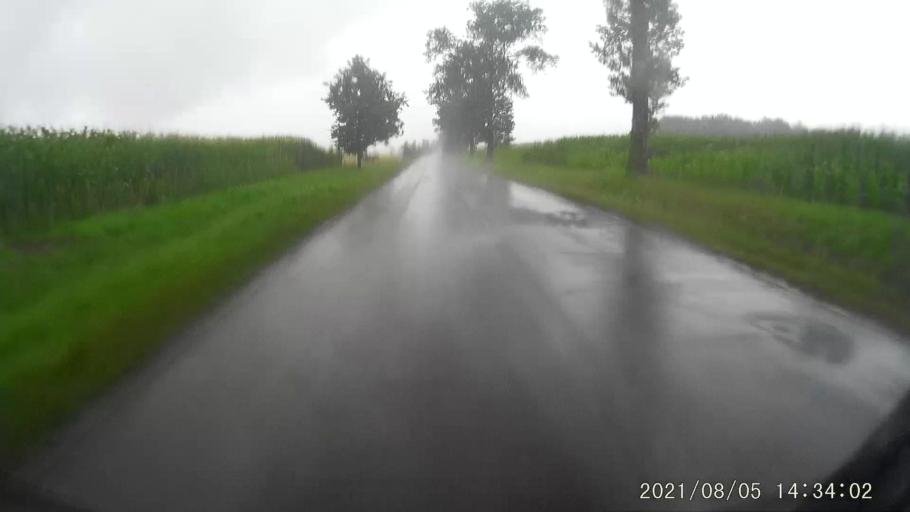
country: PL
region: Opole Voivodeship
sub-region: Powiat nyski
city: Korfantow
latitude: 50.4683
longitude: 17.5261
